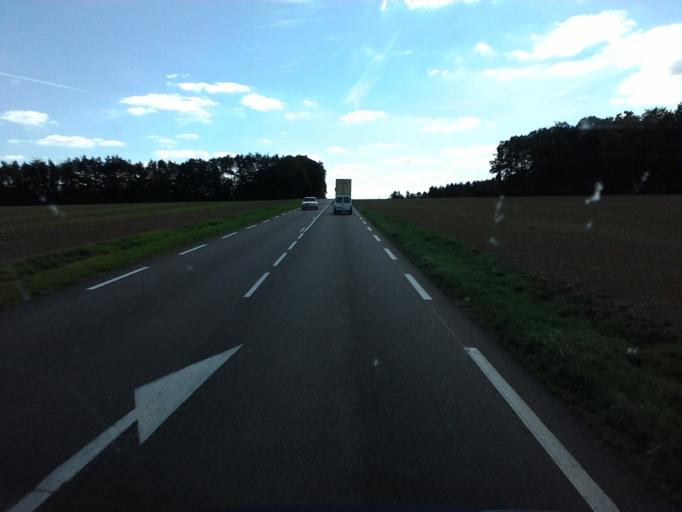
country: FR
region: Bourgogne
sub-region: Departement de la Cote-d'Or
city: Chatillon-sur-Seine
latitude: 47.7726
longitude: 4.5055
